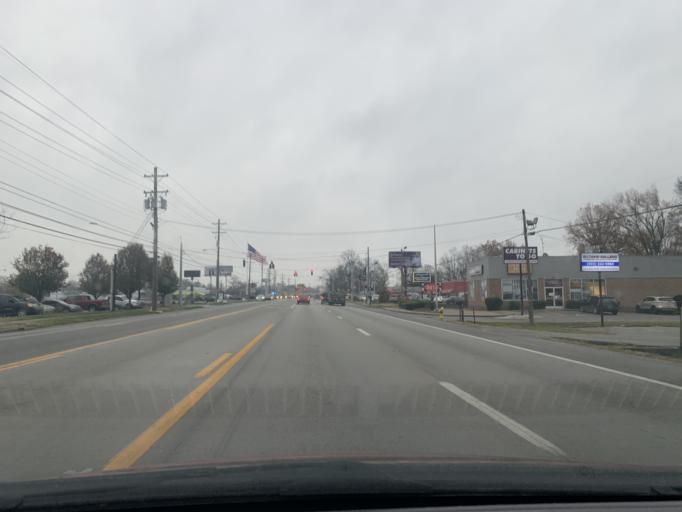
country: US
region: Kentucky
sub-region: Jefferson County
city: Okolona
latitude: 38.1657
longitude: -85.7034
